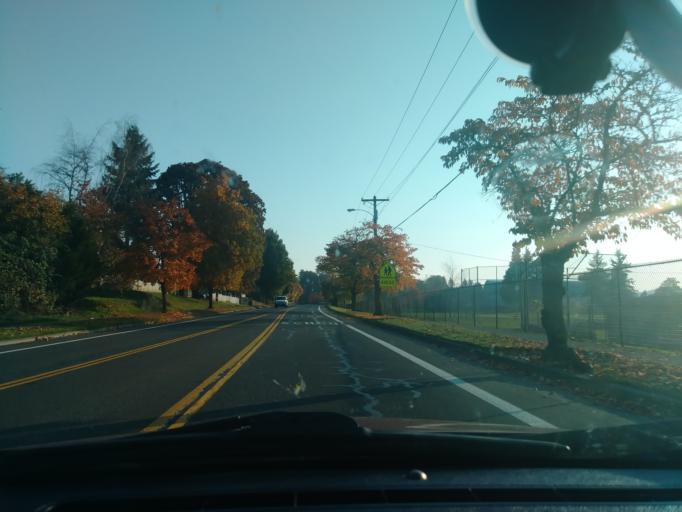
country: US
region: Oregon
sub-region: Washington County
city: Forest Grove
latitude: 45.5233
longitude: -123.1217
